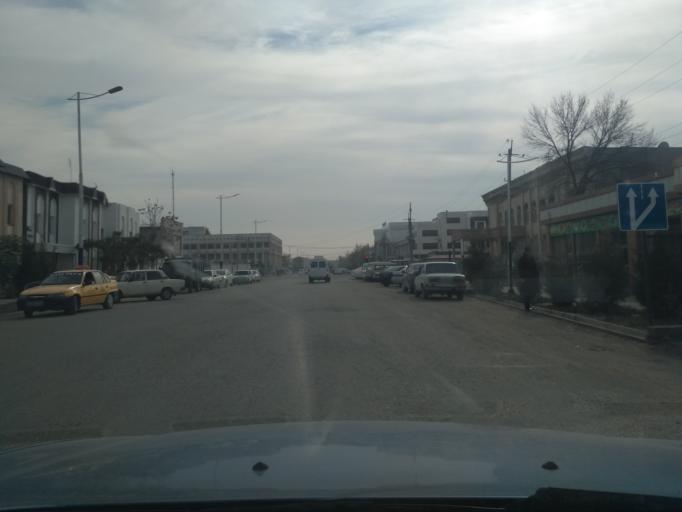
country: UZ
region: Sirdaryo
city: Guliston
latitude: 40.4998
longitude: 68.7724
